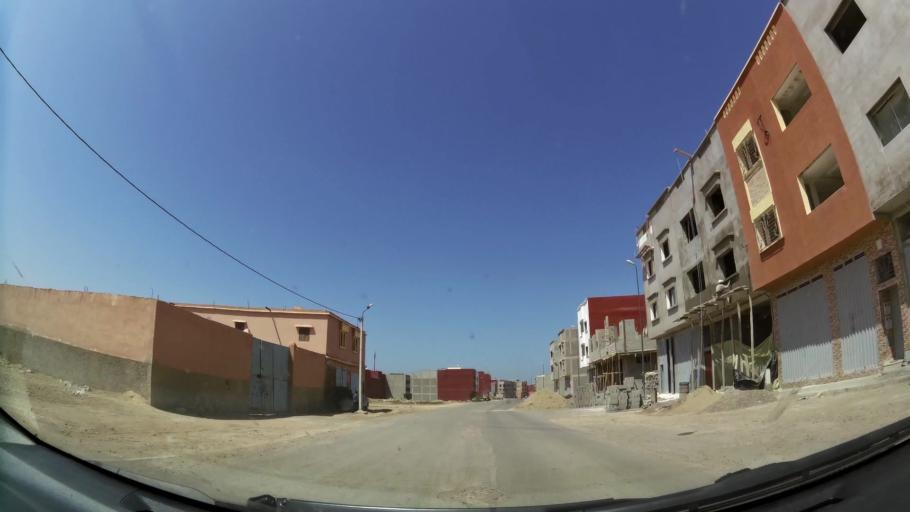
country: MA
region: Souss-Massa-Draa
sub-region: Inezgane-Ait Mellou
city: Inezgane
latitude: 30.3174
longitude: -9.5057
